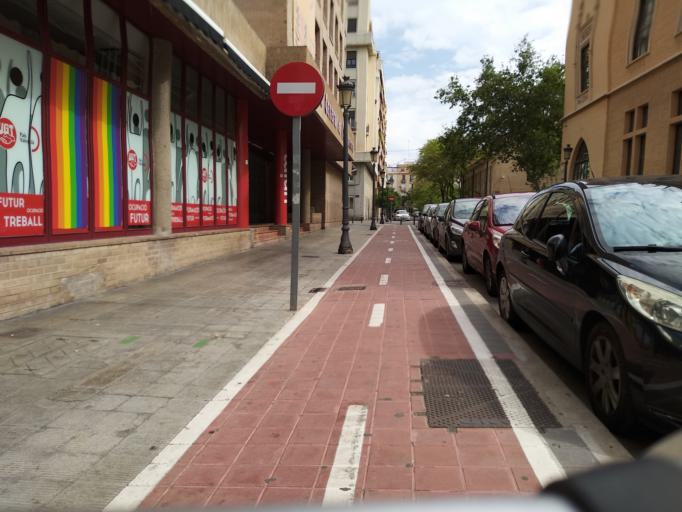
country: ES
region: Valencia
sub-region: Provincia de Valencia
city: Valencia
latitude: 39.4734
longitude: -0.3629
